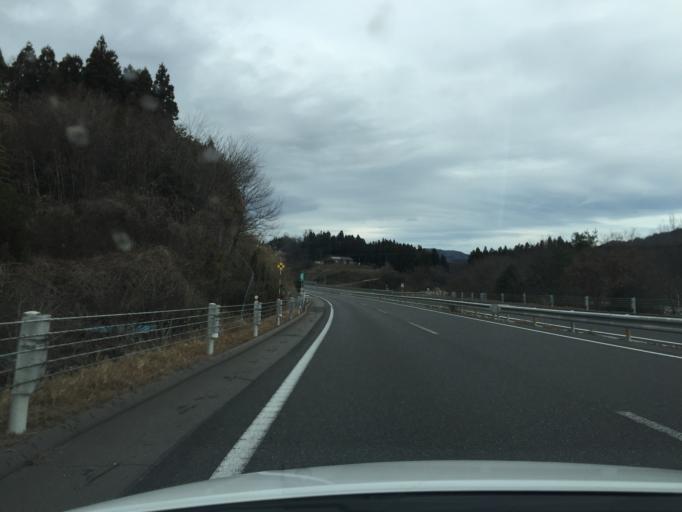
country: JP
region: Fukushima
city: Funehikimachi-funehiki
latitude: 37.2965
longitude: 140.6144
